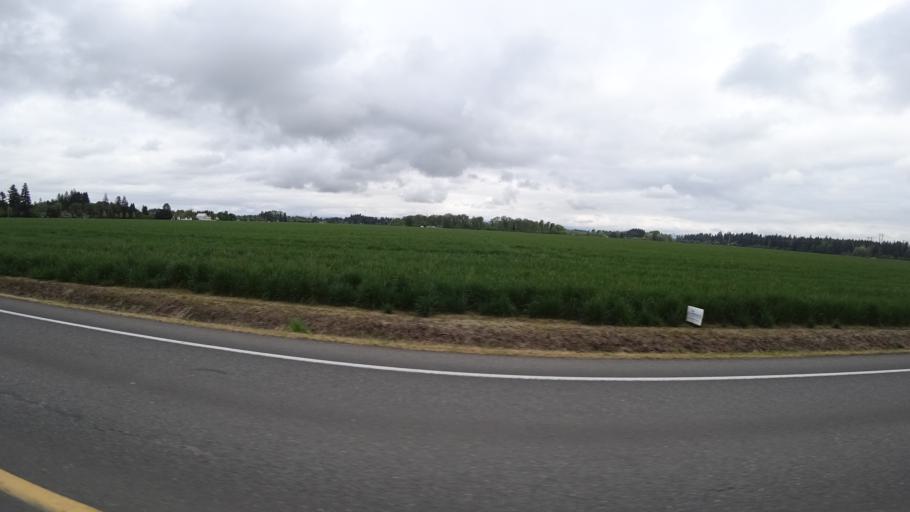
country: US
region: Oregon
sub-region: Washington County
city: Hillsboro
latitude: 45.5540
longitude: -122.9733
